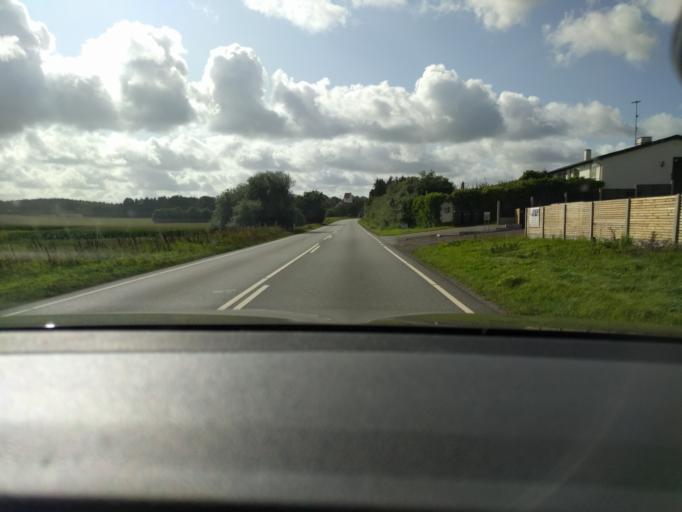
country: DK
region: Central Jutland
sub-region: Viborg Kommune
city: Bjerringbro
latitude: 56.2787
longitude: 9.6268
